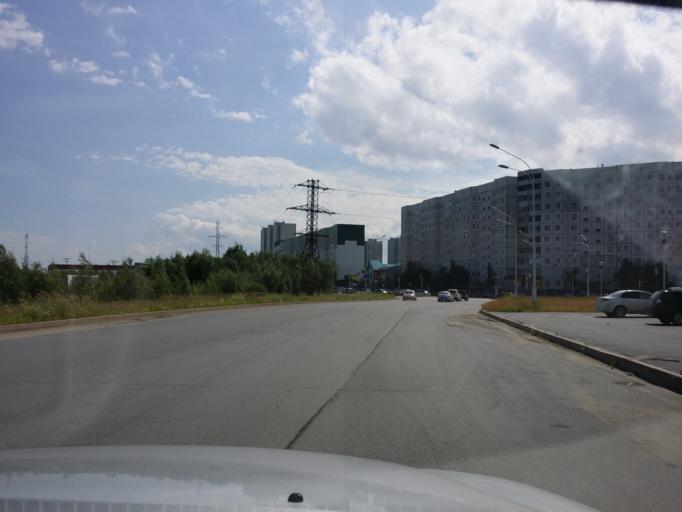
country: RU
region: Khanty-Mansiyskiy Avtonomnyy Okrug
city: Nizhnevartovsk
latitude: 60.9572
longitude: 76.5819
